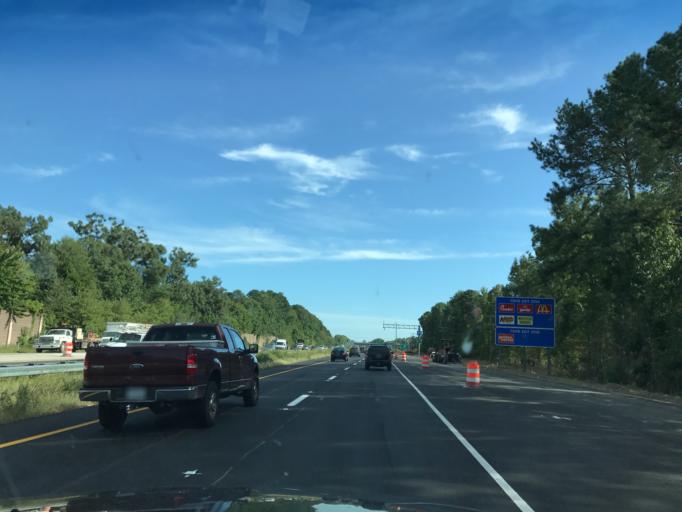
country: US
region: Virginia
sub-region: York County
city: Yorktown
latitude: 37.1329
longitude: -76.5241
